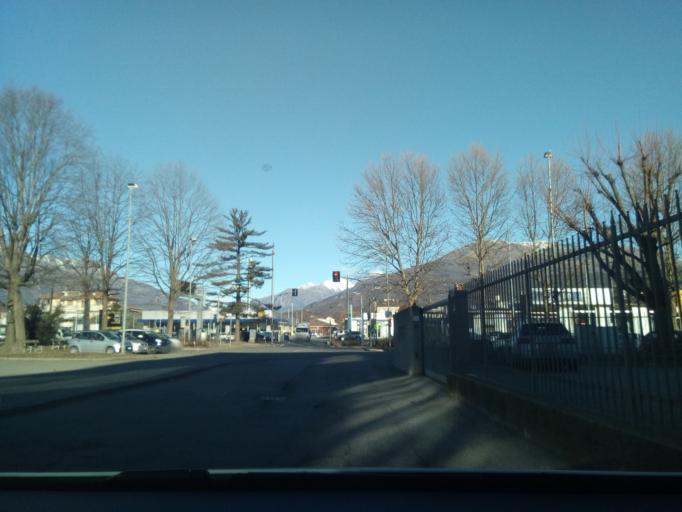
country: IT
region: Piedmont
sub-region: Provincia di Torino
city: Cascinette d'Ivrea
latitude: 45.4689
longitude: 7.9043
